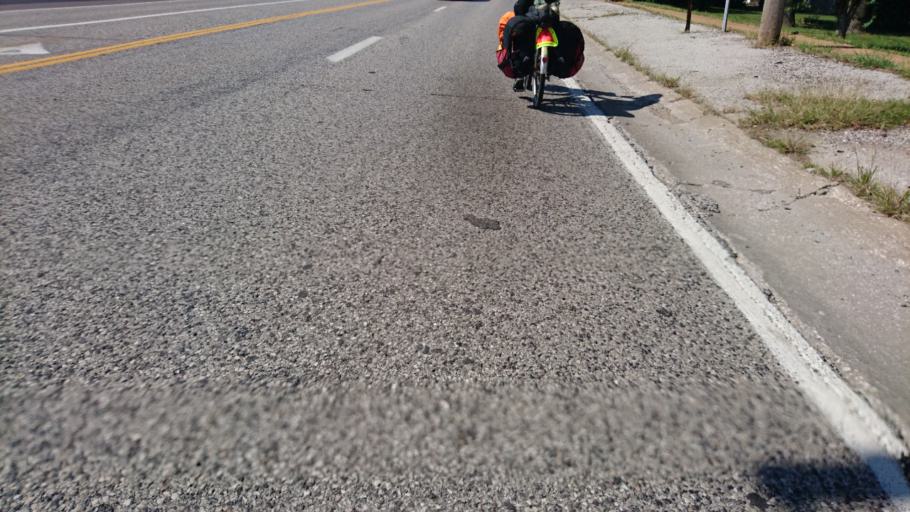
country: US
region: Missouri
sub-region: Saint Louis County
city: Des Peres
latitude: 38.5995
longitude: -90.4245
